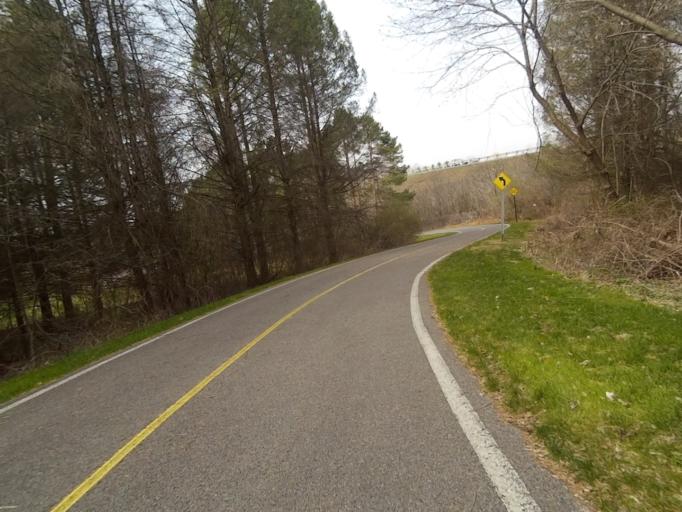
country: US
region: Pennsylvania
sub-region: Centre County
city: Lemont
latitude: 40.7923
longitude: -77.8175
